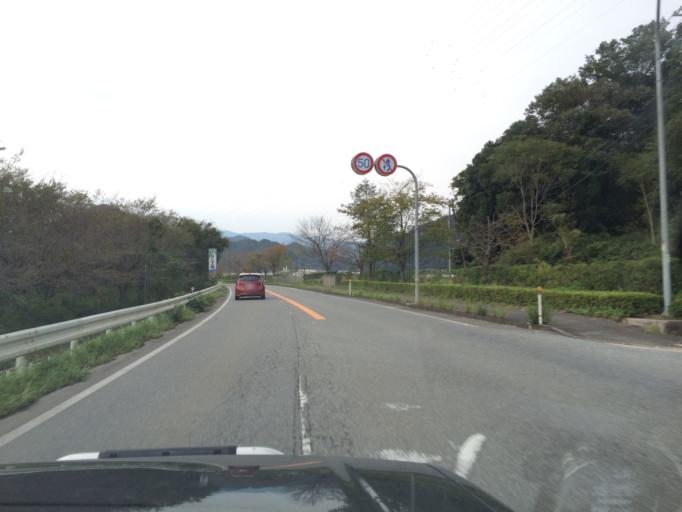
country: JP
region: Hyogo
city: Toyooka
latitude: 35.3900
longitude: 134.8101
